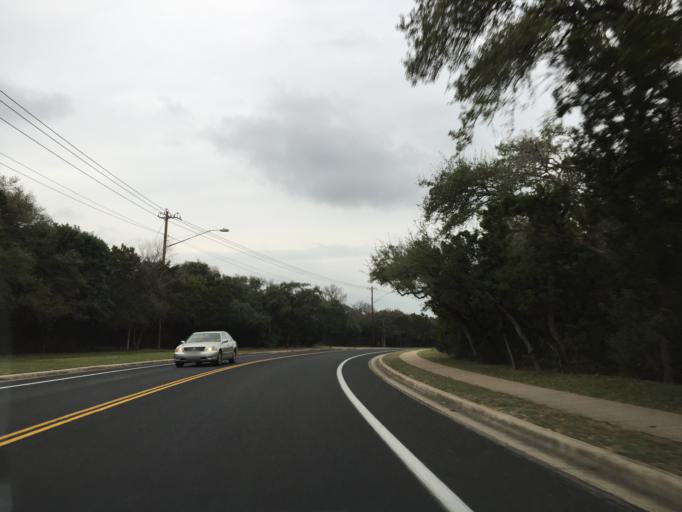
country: US
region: Texas
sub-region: Travis County
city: Barton Creek
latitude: 30.2479
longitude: -97.8417
